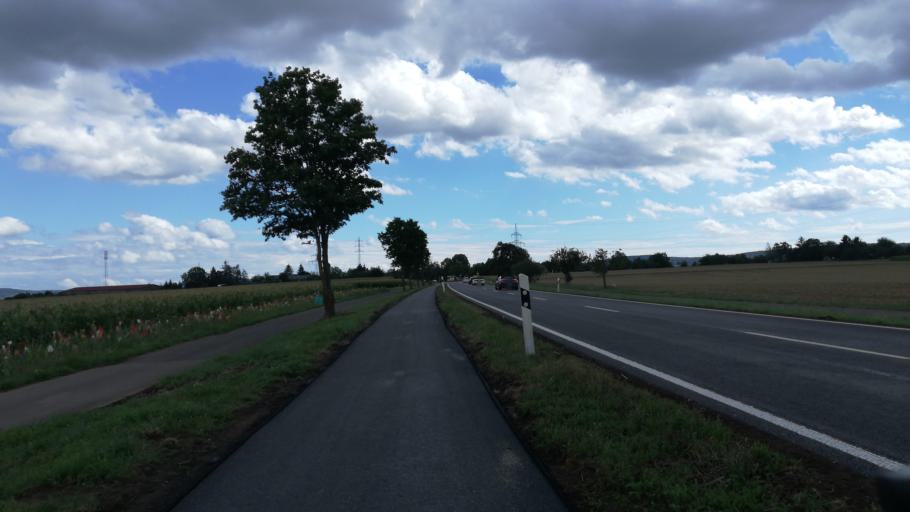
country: DE
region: Baden-Wuerttemberg
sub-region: Regierungsbezirk Stuttgart
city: Waiblingen
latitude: 48.8493
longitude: 9.3003
